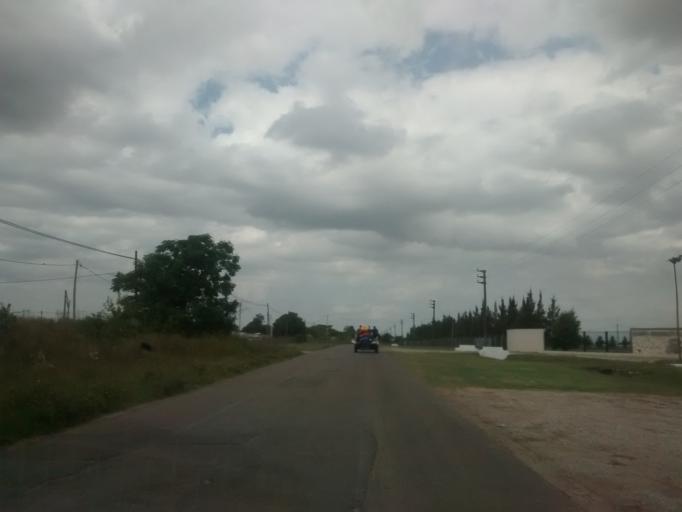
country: AR
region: Buenos Aires
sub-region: Partido de La Plata
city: La Plata
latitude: -34.9835
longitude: -57.9267
